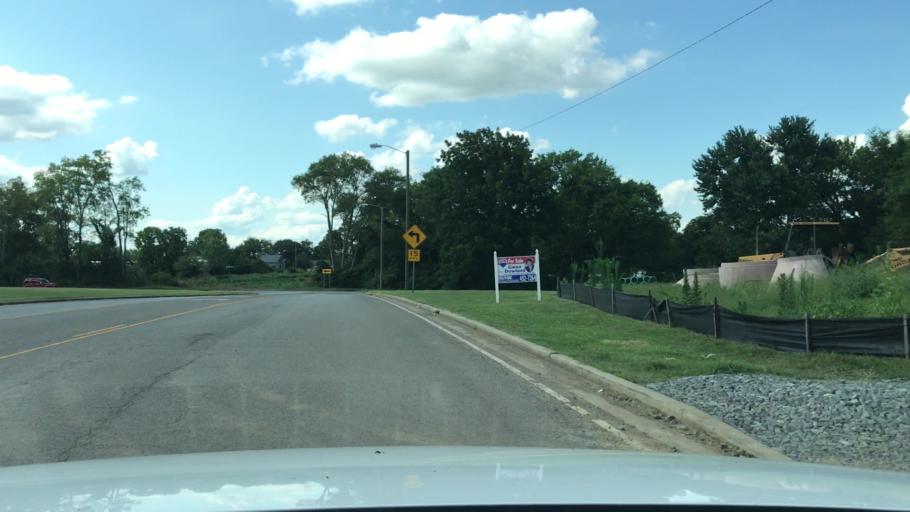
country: US
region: Tennessee
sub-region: Sumner County
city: Gallatin
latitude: 36.3842
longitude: -86.4593
